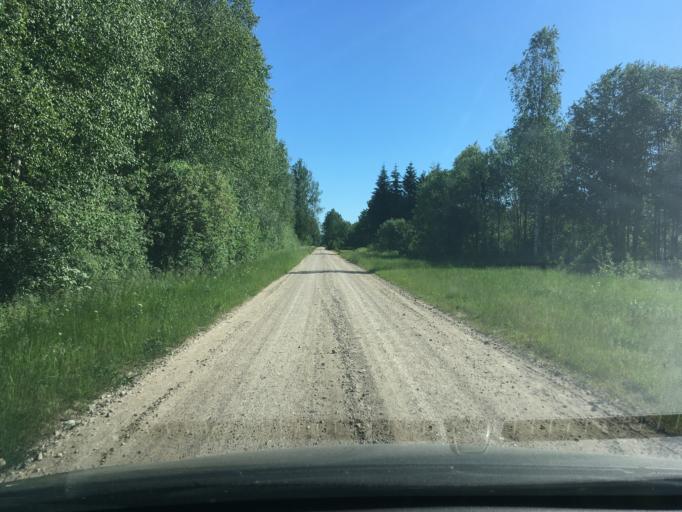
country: EE
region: Laeaene
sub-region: Lihula vald
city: Lihula
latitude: 58.6450
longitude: 23.7777
